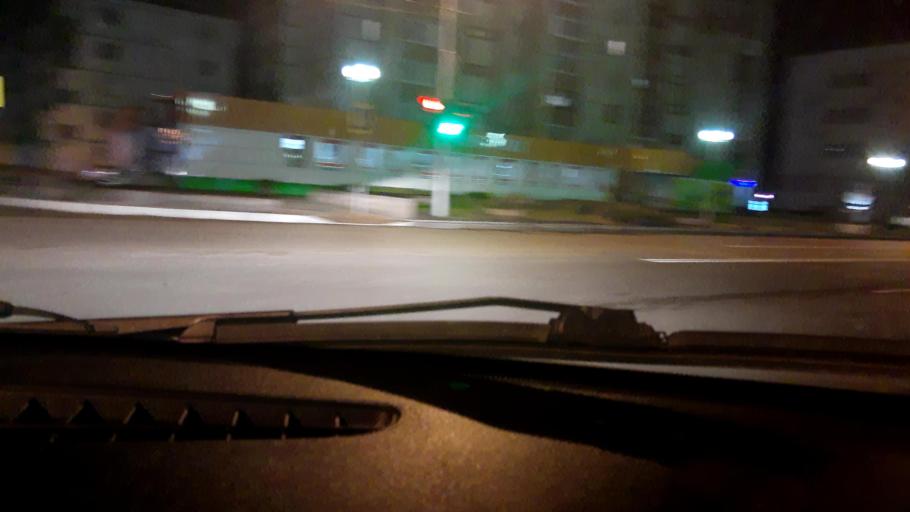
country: RU
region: Bashkortostan
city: Mikhaylovka
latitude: 54.7035
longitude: 55.8362
